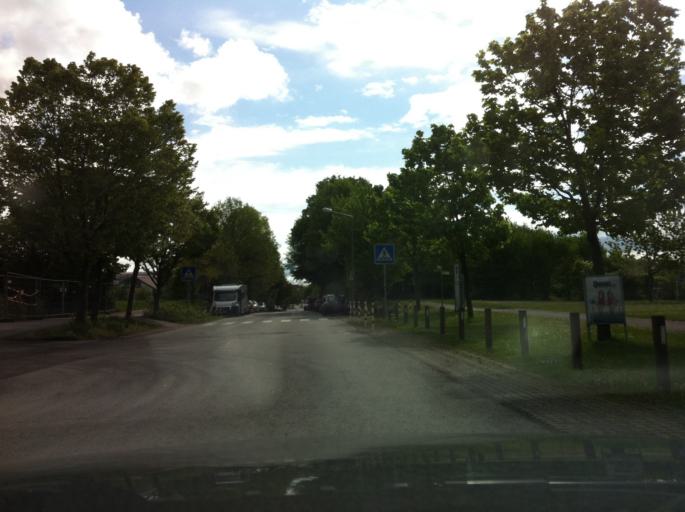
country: DE
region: Bavaria
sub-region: Upper Bavaria
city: Taufkirchen
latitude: 48.0463
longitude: 11.6086
